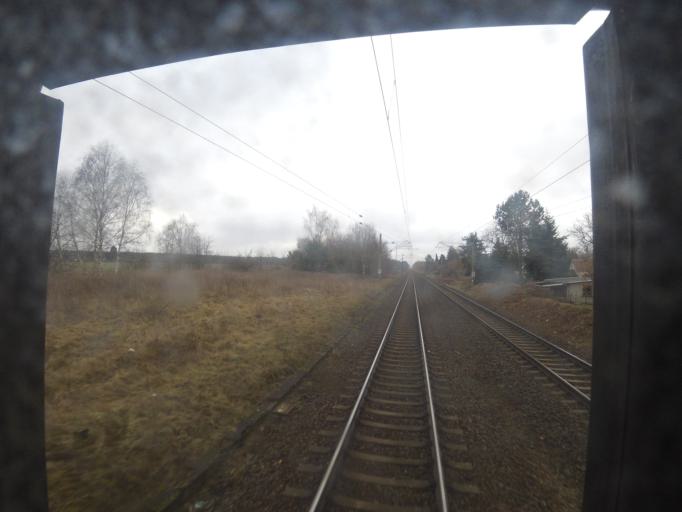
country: DE
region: Brandenburg
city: Rangsdorf
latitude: 52.3241
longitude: 13.4206
